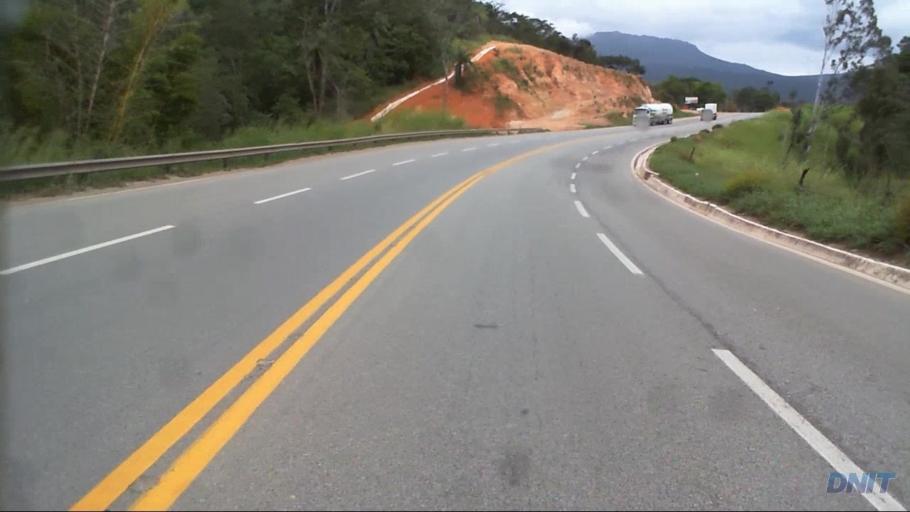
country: BR
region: Minas Gerais
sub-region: Caete
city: Caete
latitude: -19.7731
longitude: -43.6504
